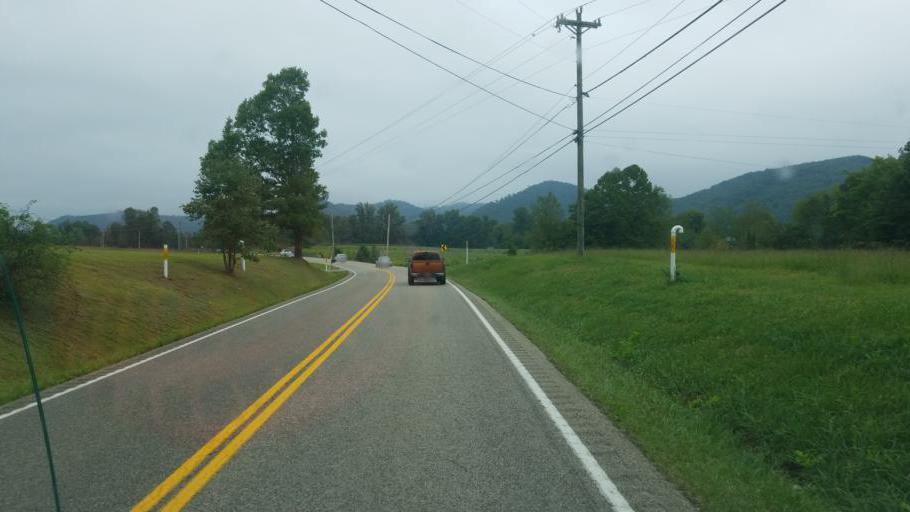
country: US
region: Kentucky
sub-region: Rowan County
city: Morehead
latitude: 38.2311
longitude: -83.4555
